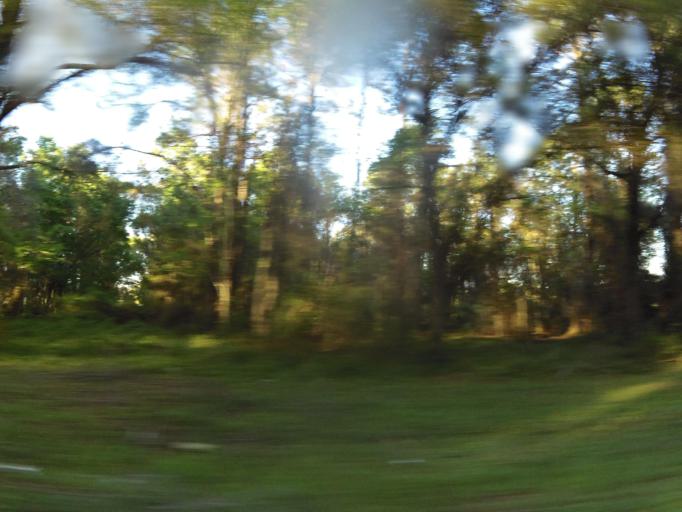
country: US
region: Florida
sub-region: Clay County
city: Keystone Heights
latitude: 29.8488
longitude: -82.0867
